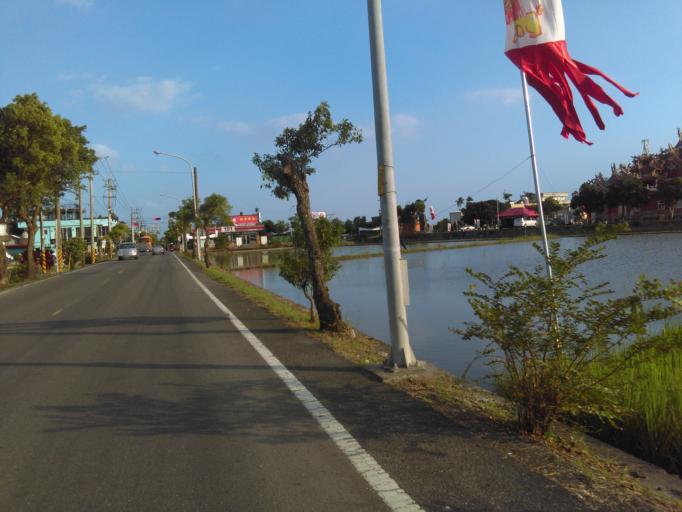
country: TW
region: Taiwan
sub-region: Yilan
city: Yilan
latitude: 24.7989
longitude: 121.7859
